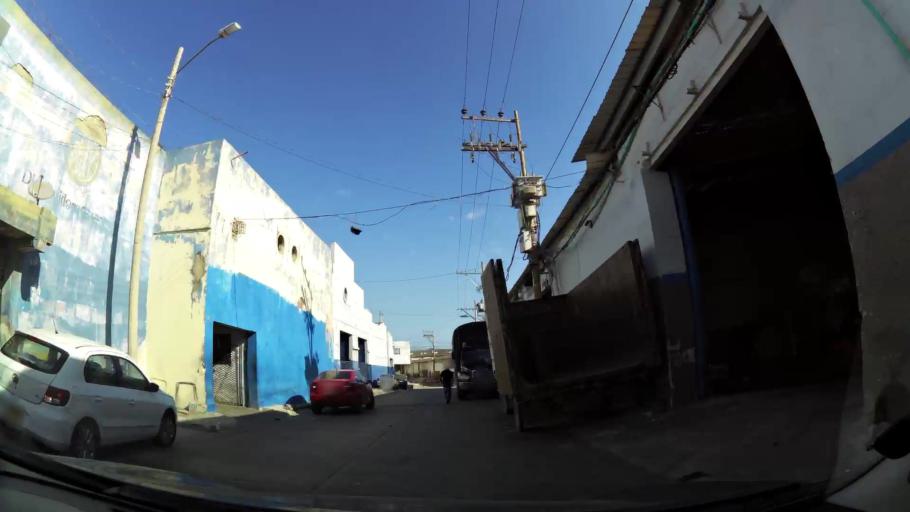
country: CO
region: Atlantico
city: Barranquilla
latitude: 10.9901
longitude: -74.7802
